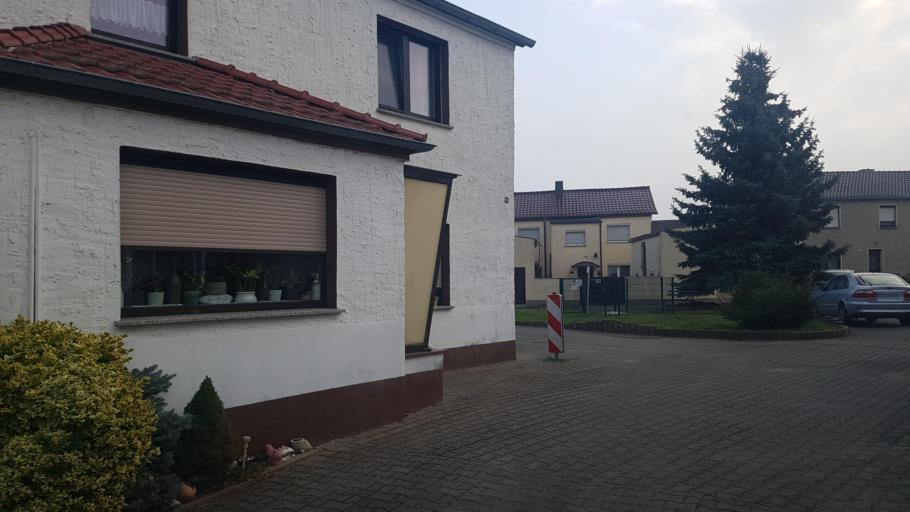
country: DE
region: Saxony-Anhalt
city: Prettin
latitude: 51.6442
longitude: 12.9841
